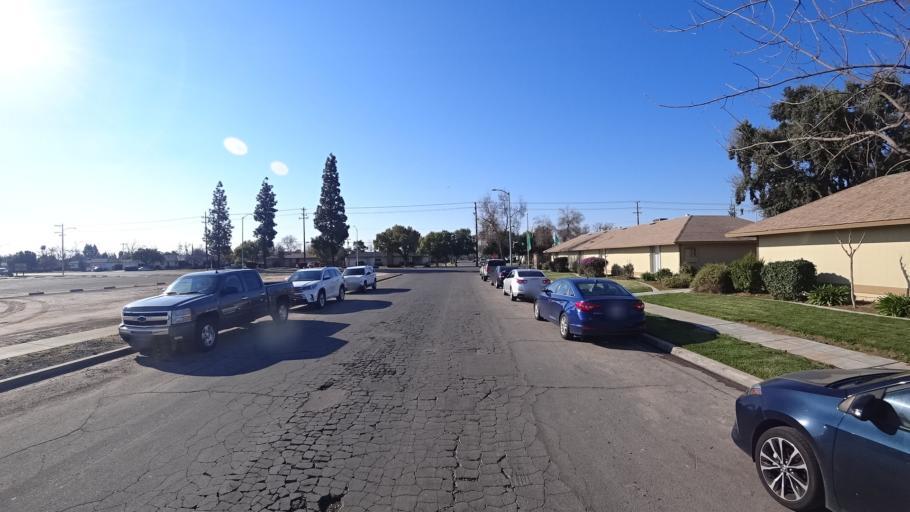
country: US
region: California
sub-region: Fresno County
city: Clovis
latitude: 36.8236
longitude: -119.7770
